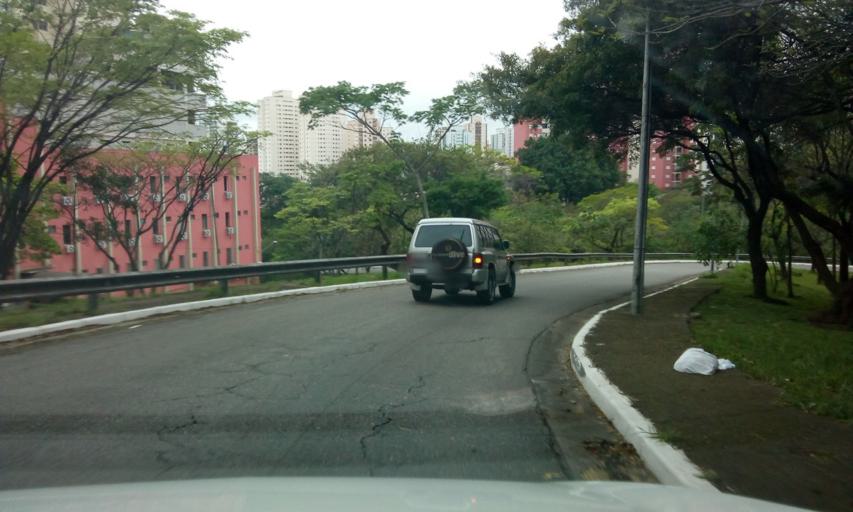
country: BR
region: Sao Paulo
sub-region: Diadema
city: Diadema
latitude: -23.6278
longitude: -46.6405
